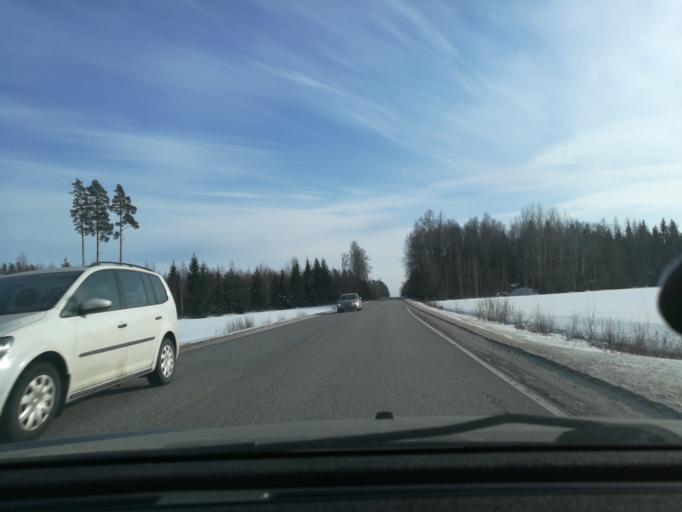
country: FI
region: Uusimaa
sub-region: Helsinki
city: Saukkola
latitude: 60.4208
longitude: 24.0426
